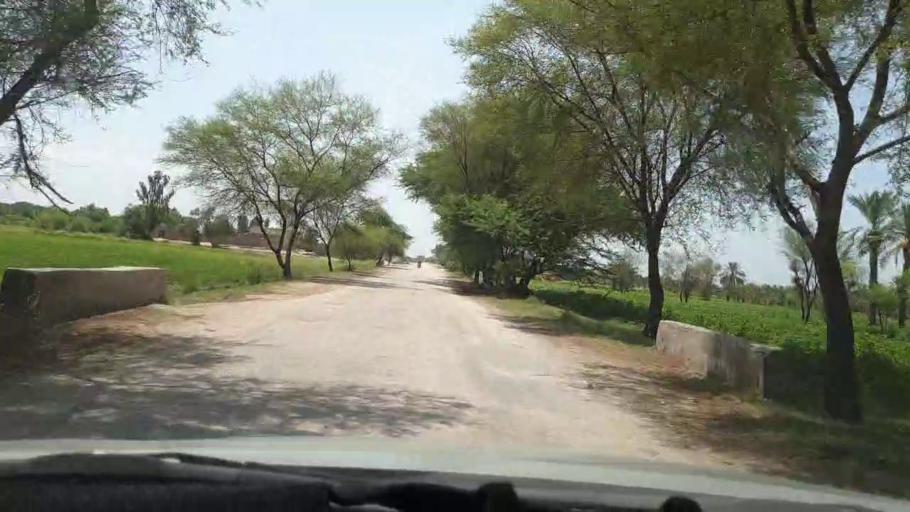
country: PK
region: Sindh
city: Pano Aqil
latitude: 27.6635
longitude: 69.1362
